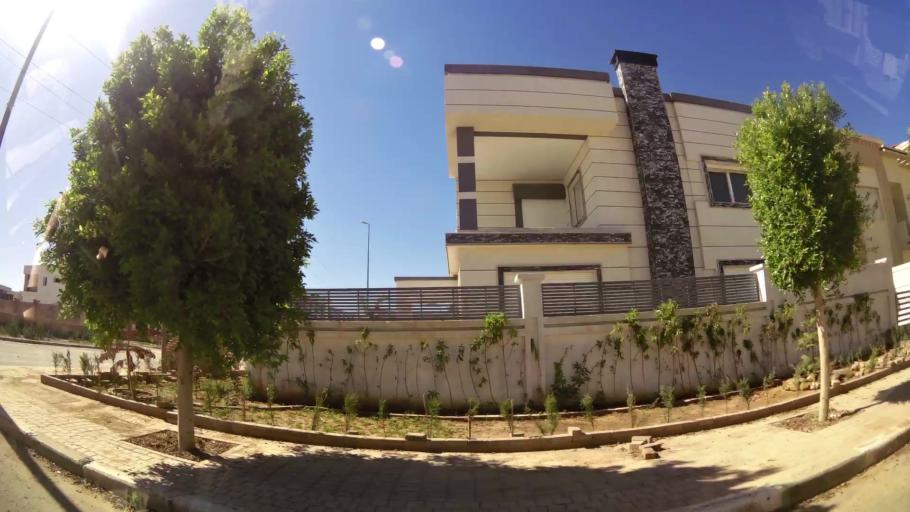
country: MA
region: Oriental
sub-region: Oujda-Angad
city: Oujda
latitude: 34.7193
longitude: -1.9161
